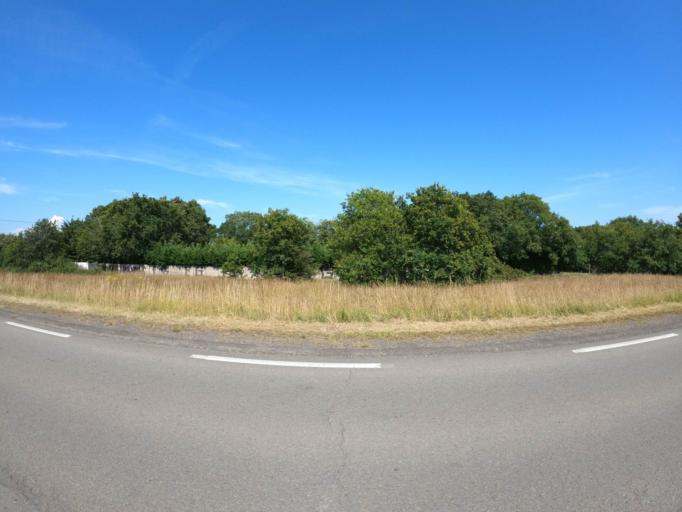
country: FR
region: Pays de la Loire
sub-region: Departement de la Loire-Atlantique
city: La Bernerie-en-Retz
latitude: 47.0949
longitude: -2.0358
